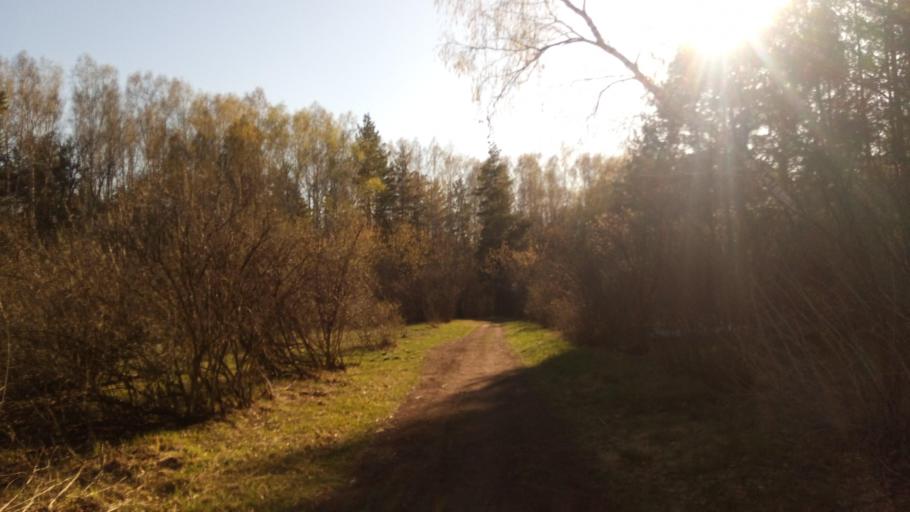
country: RU
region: Chelyabinsk
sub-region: Gorod Chelyabinsk
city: Chelyabinsk
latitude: 55.1533
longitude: 61.3486
